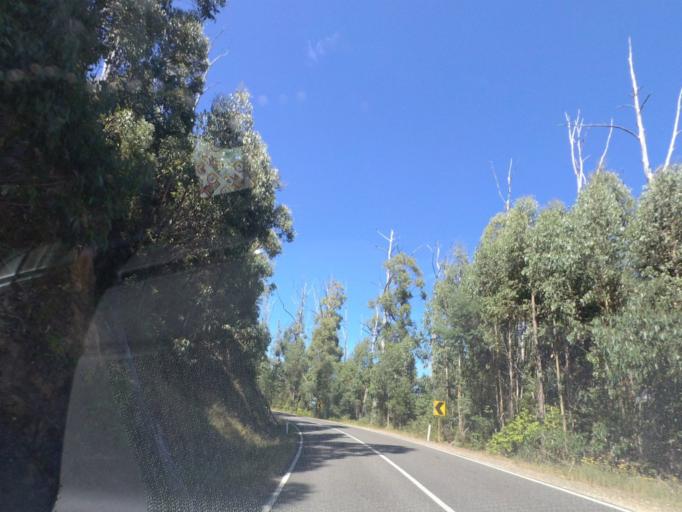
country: AU
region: Victoria
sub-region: Yarra Ranges
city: Millgrove
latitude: -37.5148
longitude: 145.7689
